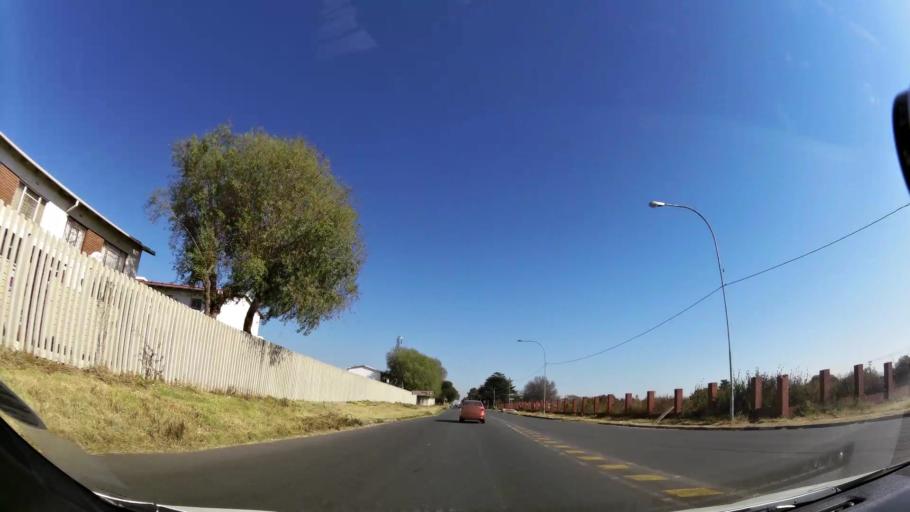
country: ZA
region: Gauteng
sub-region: City of Johannesburg Metropolitan Municipality
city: Johannesburg
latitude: -26.2437
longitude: 28.0945
